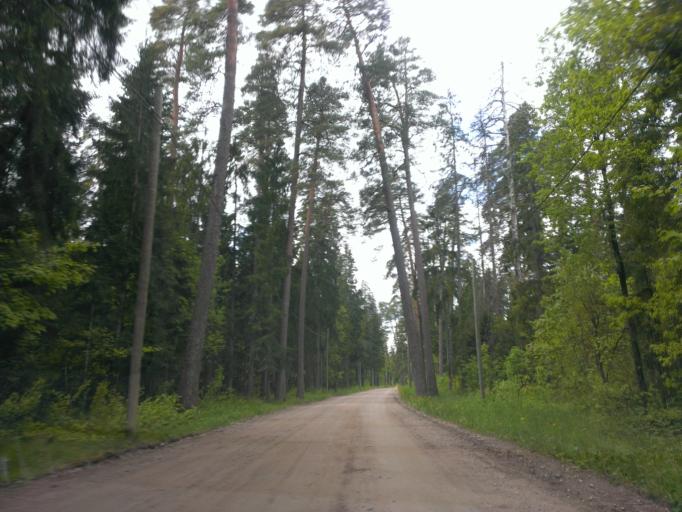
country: LV
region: Baldone
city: Baldone
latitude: 56.7414
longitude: 24.4204
